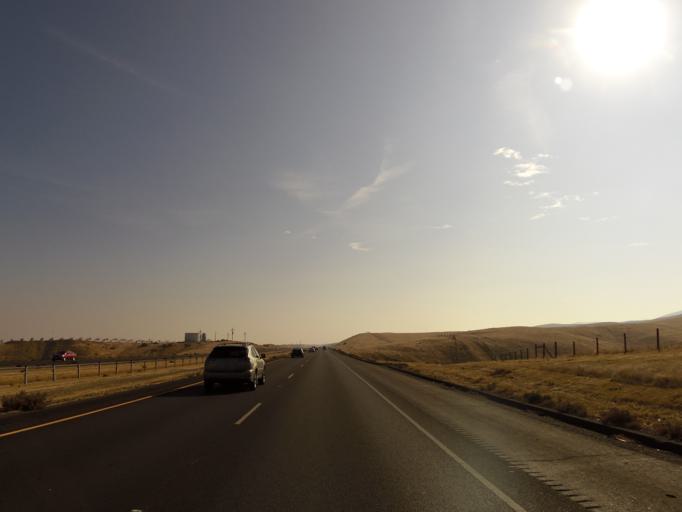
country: US
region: California
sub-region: Kings County
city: Avenal
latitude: 36.0450
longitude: -120.0494
